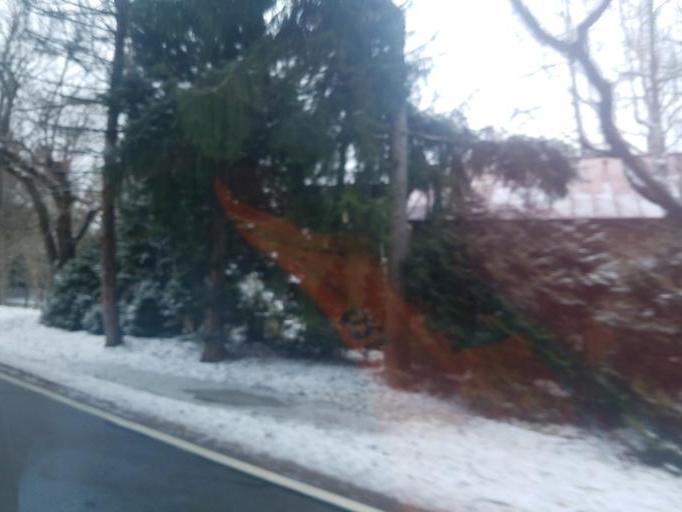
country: US
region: Ohio
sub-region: Franklin County
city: New Albany
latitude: 40.0507
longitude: -82.8042
